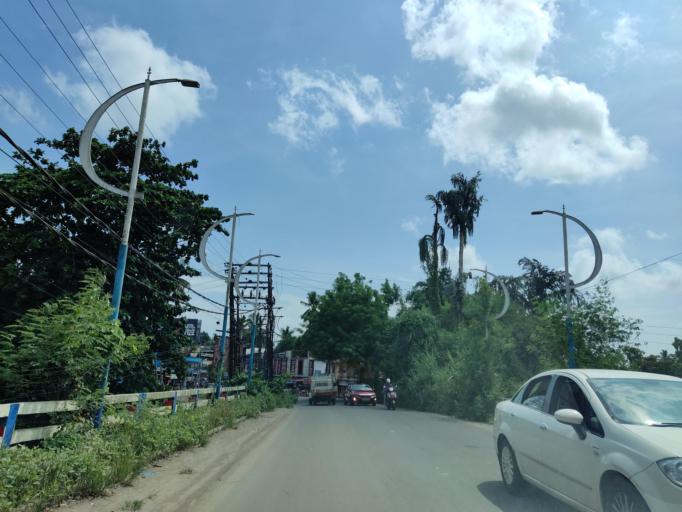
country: IN
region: Kerala
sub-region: Alappuzha
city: Mavelikara
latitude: 9.2546
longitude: 76.5482
